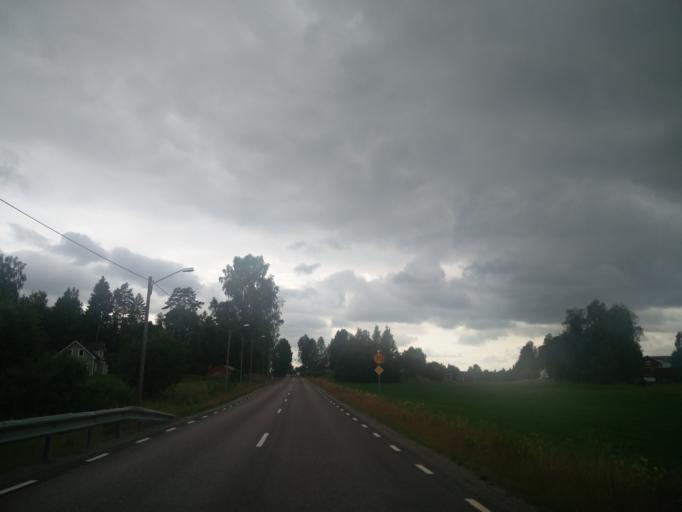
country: SE
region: Vaermland
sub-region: Arvika Kommun
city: Arvika
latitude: 59.8880
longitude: 12.6313
